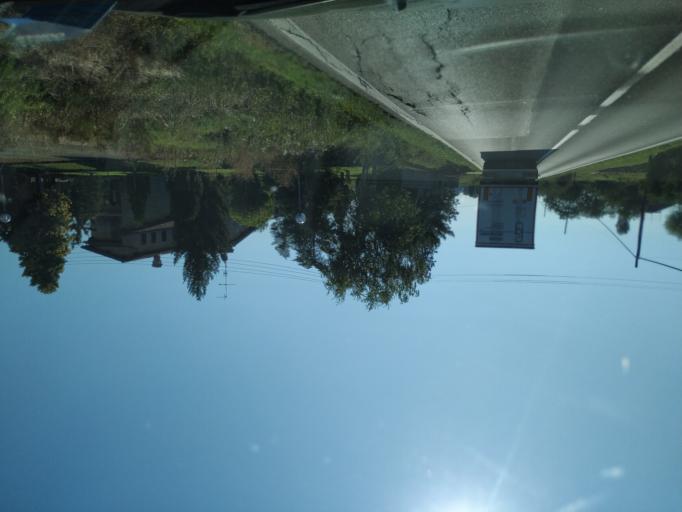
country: IT
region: Emilia-Romagna
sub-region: Provincia di Bologna
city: Sant'Agata Bolognese
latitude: 44.6540
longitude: 11.1439
